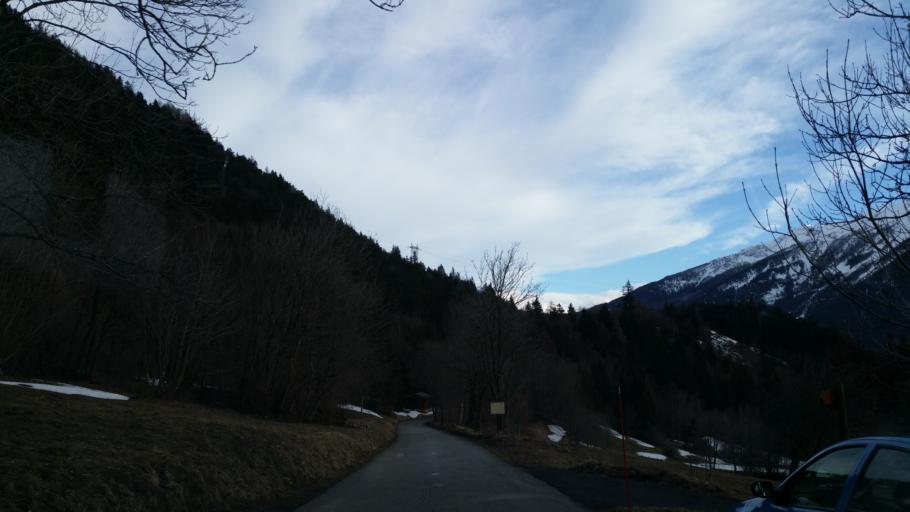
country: FR
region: Rhone-Alpes
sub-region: Departement de la Savoie
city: Villargondran
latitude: 45.2824
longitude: 6.3830
